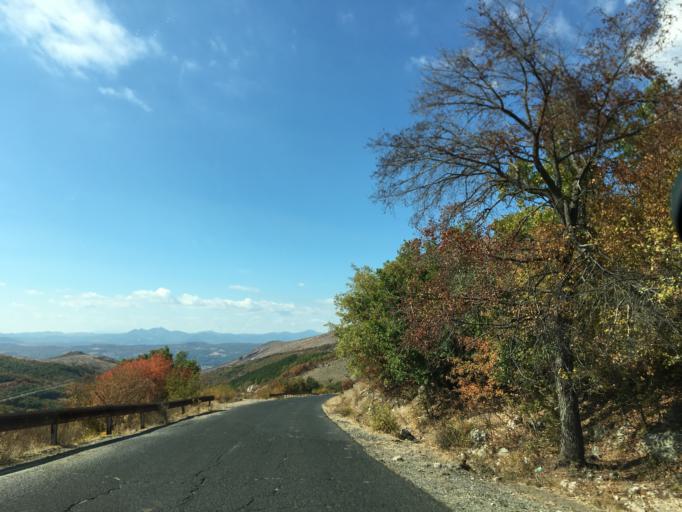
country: BG
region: Kurdzhali
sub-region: Obshtina Kurdzhali
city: Kurdzhali
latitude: 41.5312
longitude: 25.4698
